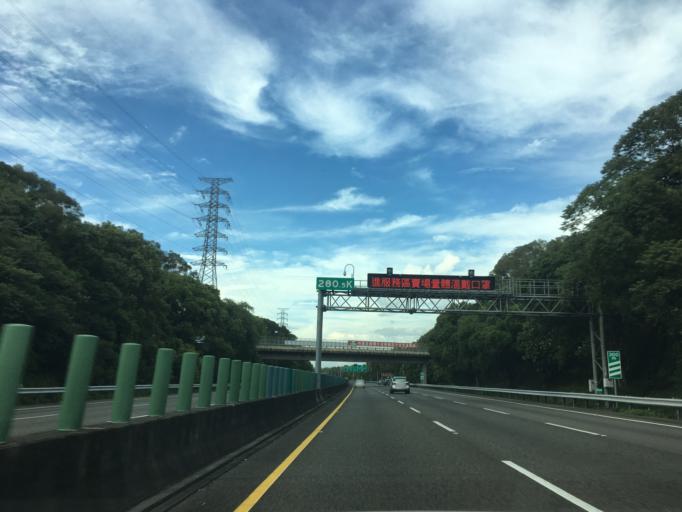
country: TW
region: Taiwan
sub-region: Yunlin
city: Douliu
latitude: 23.5863
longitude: 120.5159
